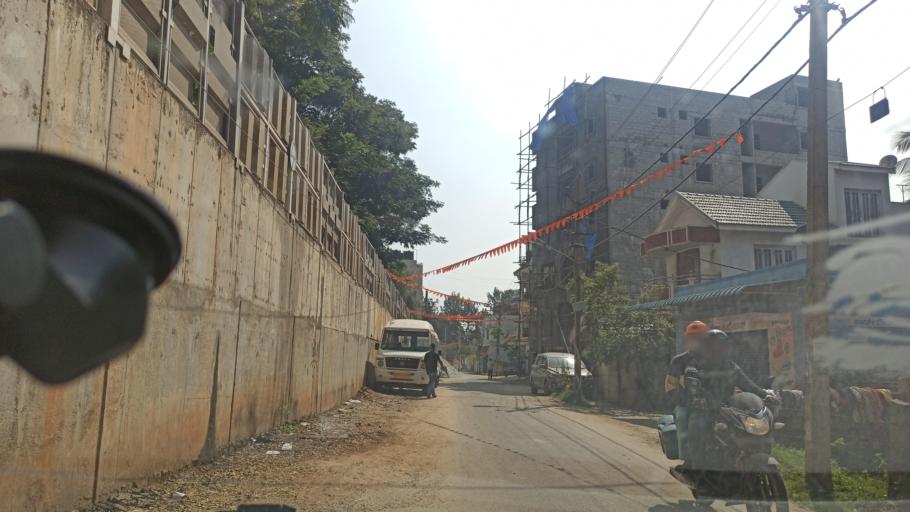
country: IN
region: Karnataka
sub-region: Bangalore Urban
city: Yelahanka
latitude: 13.0671
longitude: 77.5902
